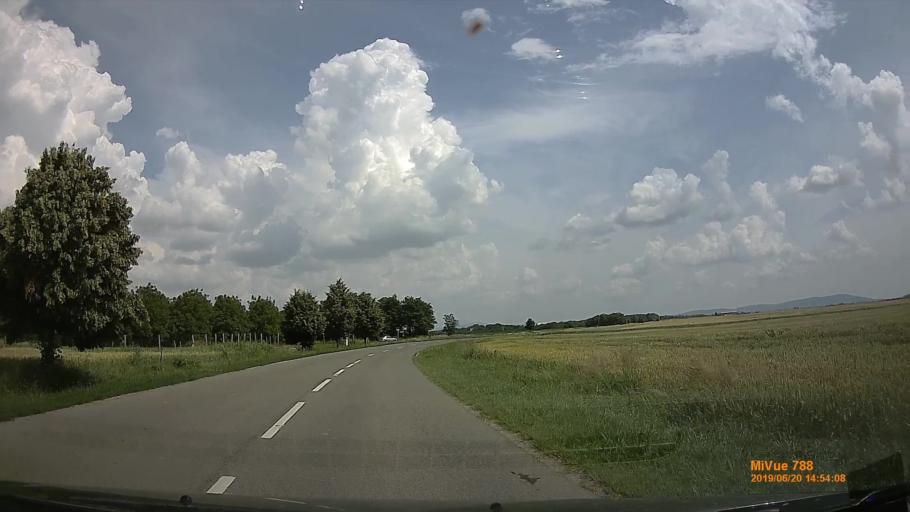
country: HU
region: Baranya
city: Kozarmisleny
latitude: 46.0022
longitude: 18.2401
